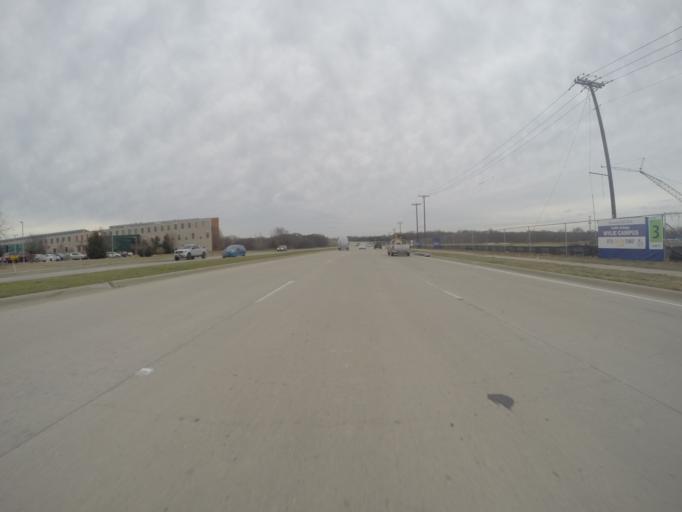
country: US
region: Texas
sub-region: Collin County
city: Saint Paul
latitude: 33.0257
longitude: -96.5689
